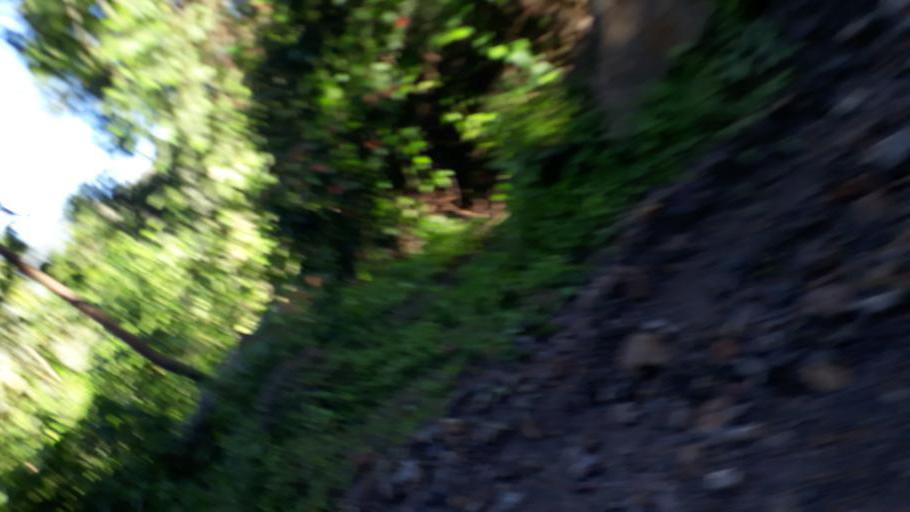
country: CO
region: Casanare
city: Nunchia
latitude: 5.6514
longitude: -72.4224
